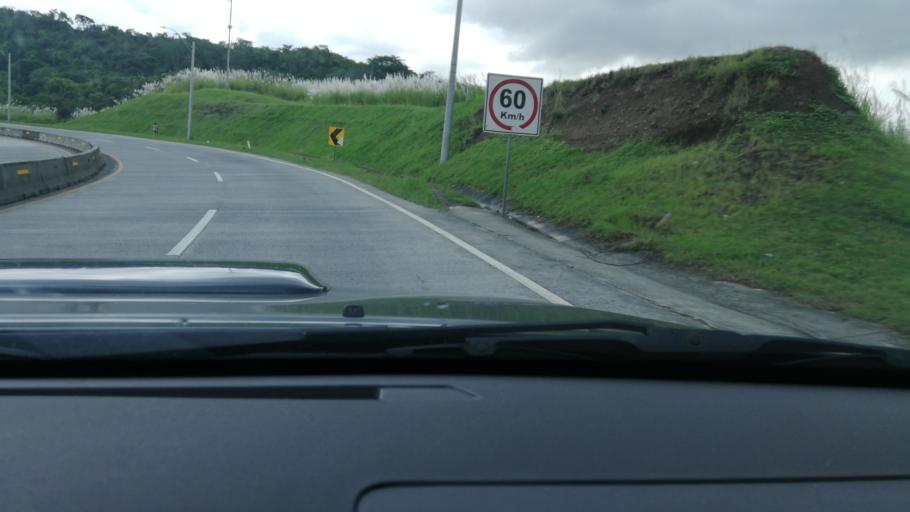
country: PA
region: Panama
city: San Miguelito
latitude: 9.0632
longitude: -79.4730
